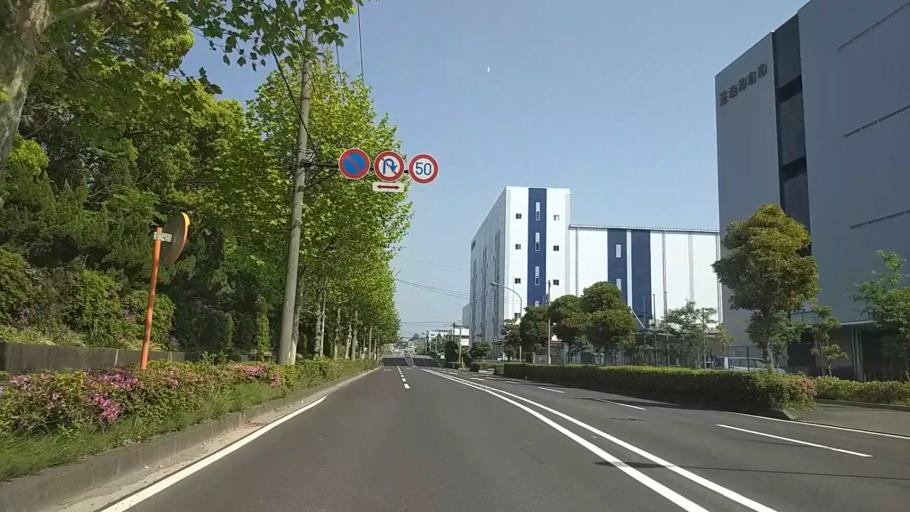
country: JP
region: Kanagawa
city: Yokohama
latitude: 35.4804
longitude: 139.6579
